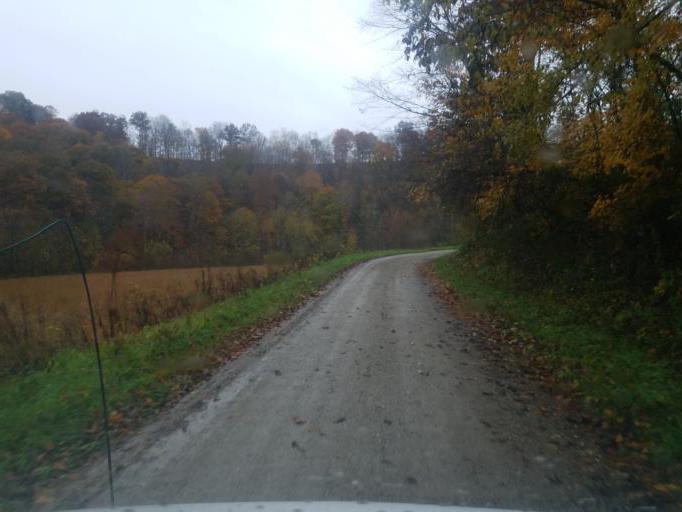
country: US
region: Ohio
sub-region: Washington County
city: Beverly
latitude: 39.4736
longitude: -81.7431
